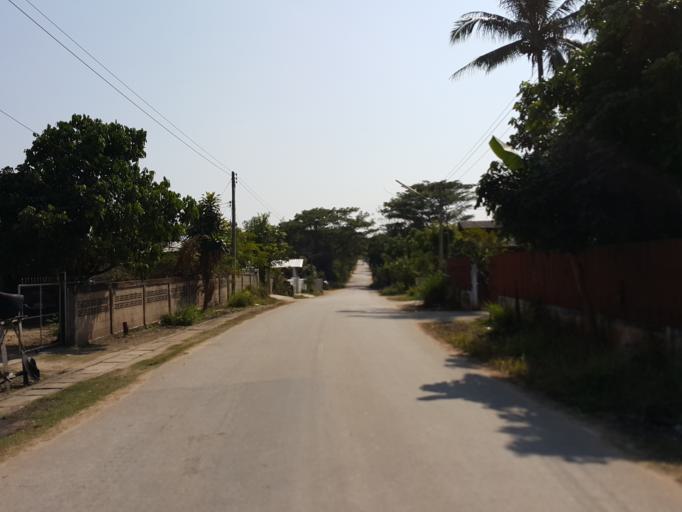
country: TH
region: Lampang
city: Wang Nuea
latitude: 19.0283
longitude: 99.6237
